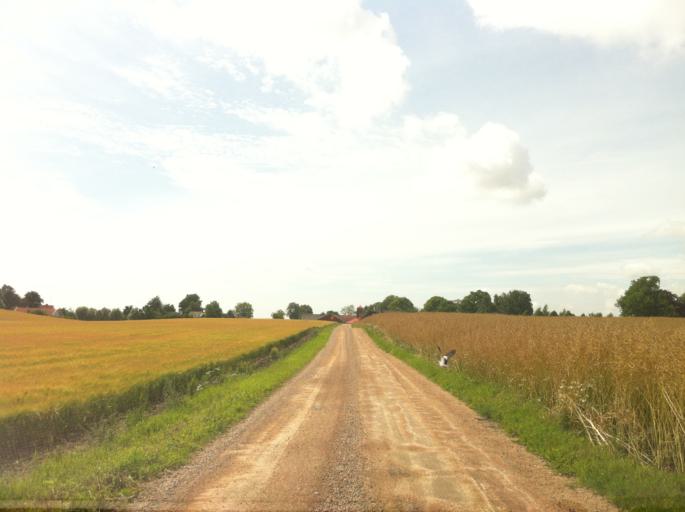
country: SE
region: Skane
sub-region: Skurups Kommun
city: Skurup
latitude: 55.4518
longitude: 13.4319
